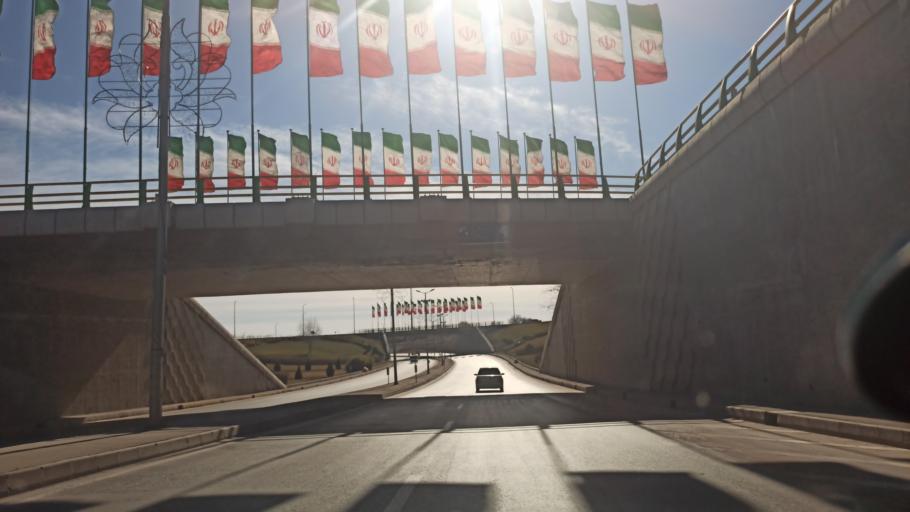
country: IR
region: Qazvin
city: Qazvin
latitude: 36.2456
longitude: 50.0016
